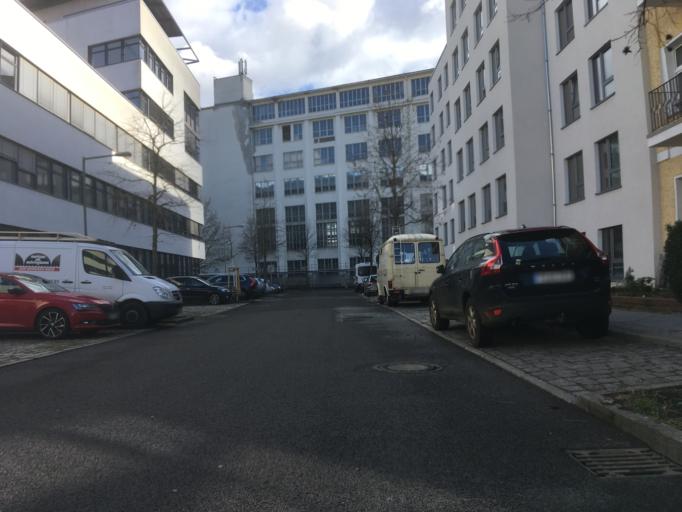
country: DE
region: Berlin
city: Oberschoneweide
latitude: 52.4577
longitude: 13.5322
